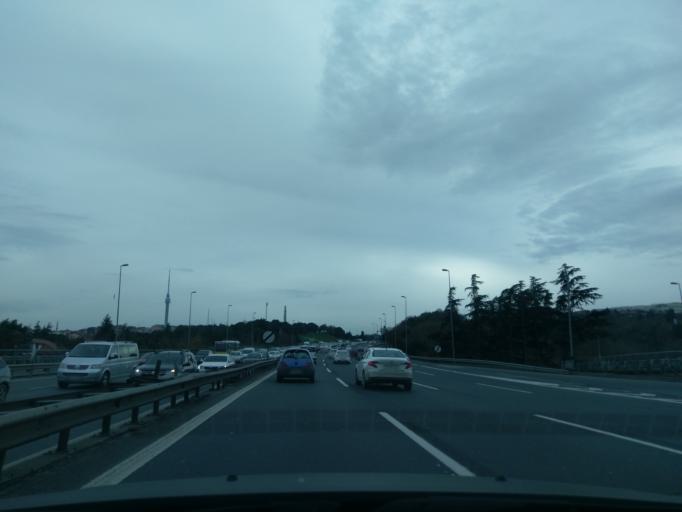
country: TR
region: Istanbul
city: UEskuedar
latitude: 41.0360
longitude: 29.0438
